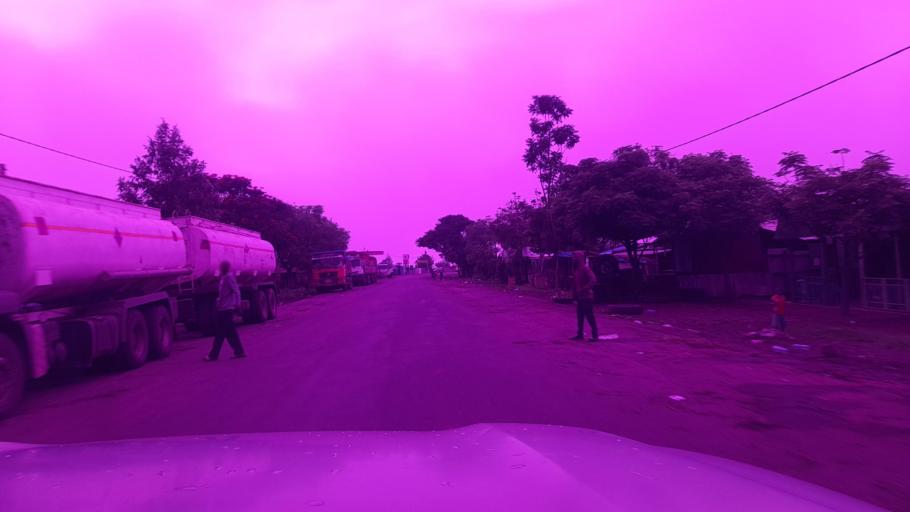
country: ET
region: Oromiya
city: Waliso
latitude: 8.1747
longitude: 37.5739
